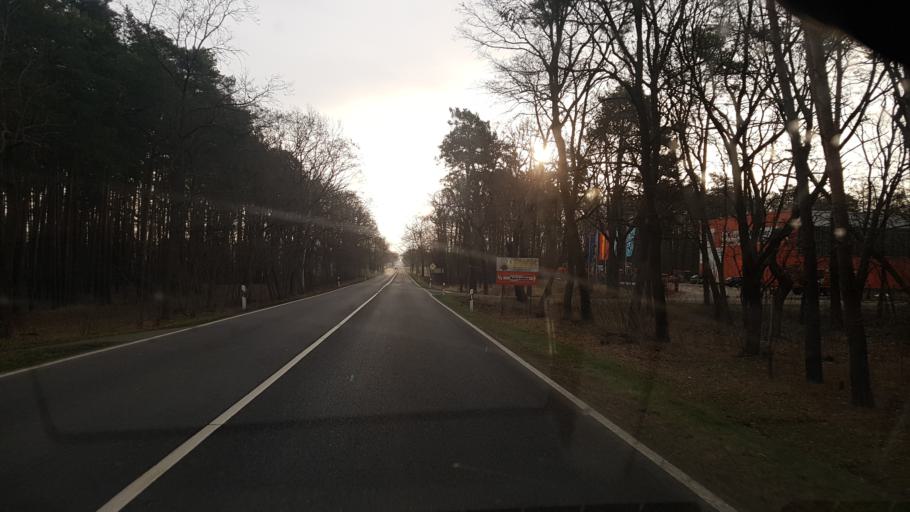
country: DE
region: Brandenburg
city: Werben
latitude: 51.7608
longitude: 14.1473
